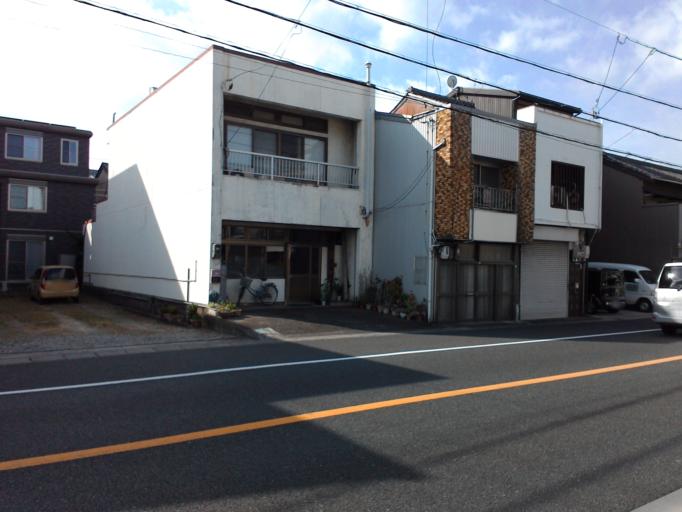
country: JP
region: Shizuoka
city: Kosai-shi
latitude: 34.6940
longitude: 137.5655
